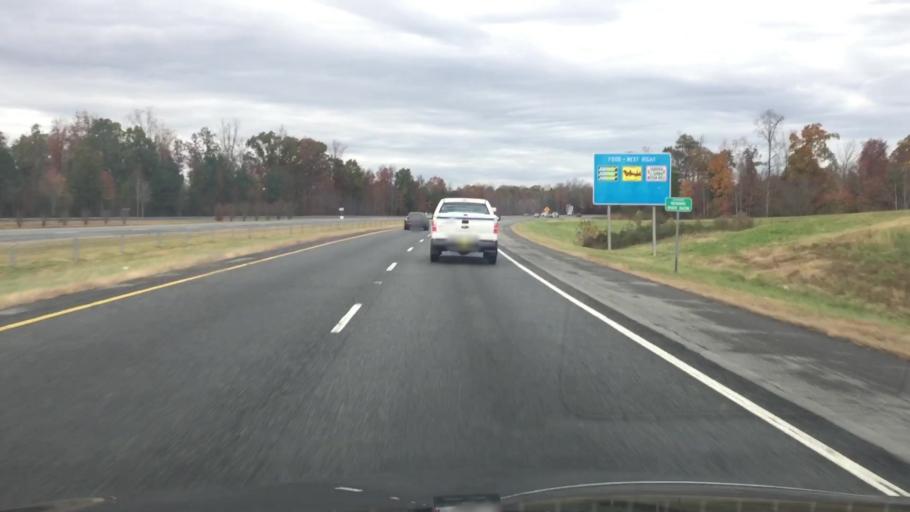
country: US
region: North Carolina
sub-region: Rockingham County
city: Reidsville
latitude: 36.3123
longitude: -79.6455
